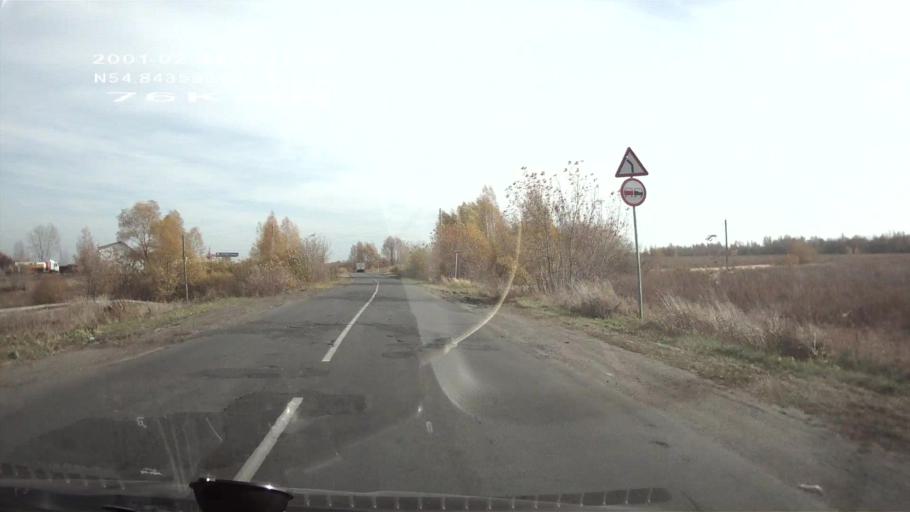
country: RU
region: Chuvashia
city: Alatyr'
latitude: 54.8436
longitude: 46.4718
